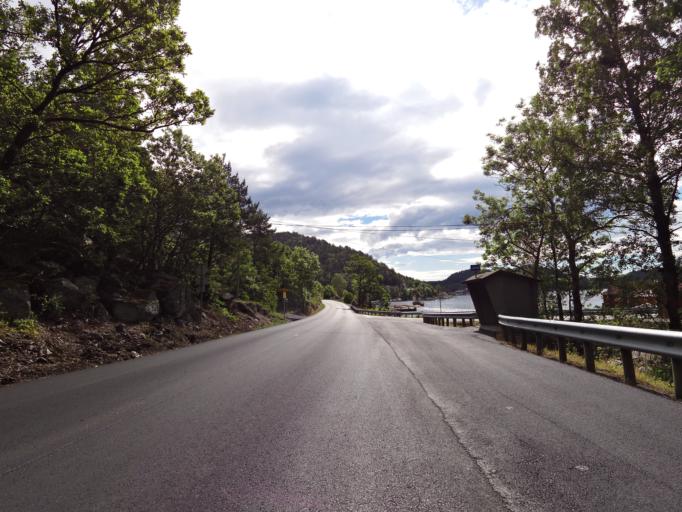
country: NO
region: Vest-Agder
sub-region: Lindesnes
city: Vigeland
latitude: 58.0515
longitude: 7.2441
